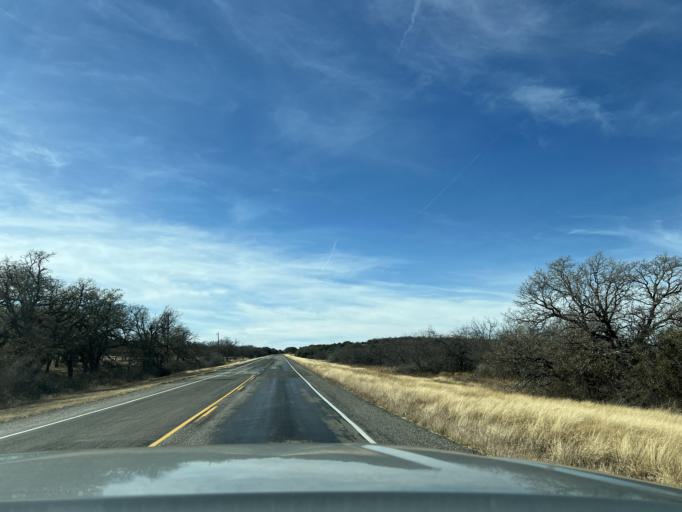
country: US
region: Texas
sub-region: Eastland County
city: Cisco
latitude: 32.4646
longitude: -99.0232
